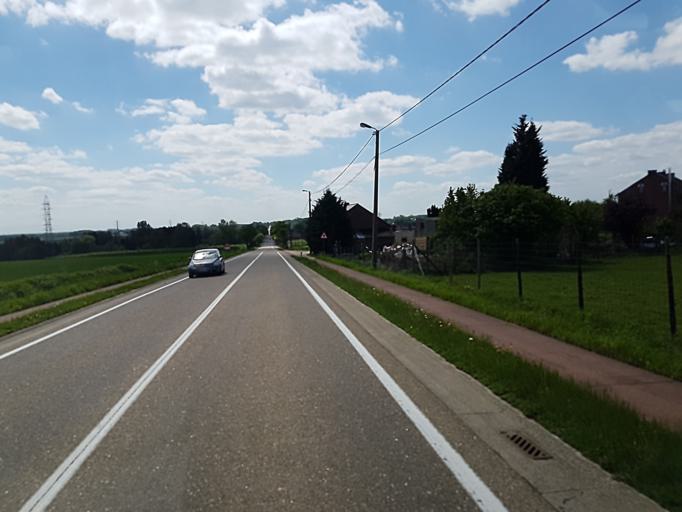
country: BE
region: Flanders
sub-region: Provincie Vlaams-Brabant
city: Glabbeek-Zuurbemde
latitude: 50.9007
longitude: 4.9736
